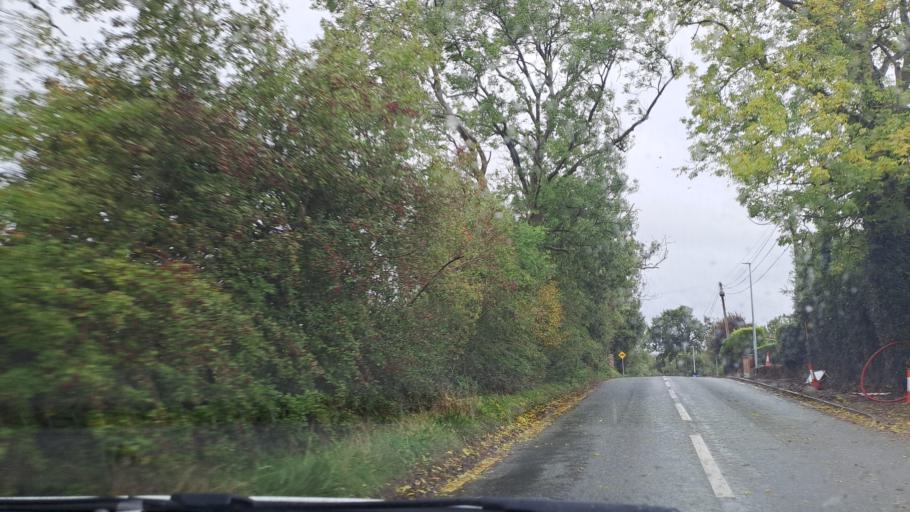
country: IE
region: Leinster
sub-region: Lu
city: Dundalk
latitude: 53.9706
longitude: -6.4847
